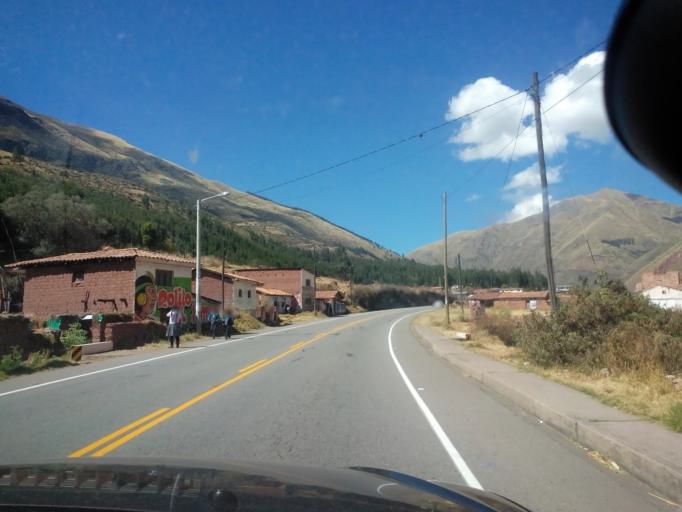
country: PE
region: Cusco
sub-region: Provincia de Quispicanchis
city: Cusipata
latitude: -13.9598
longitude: -71.4964
